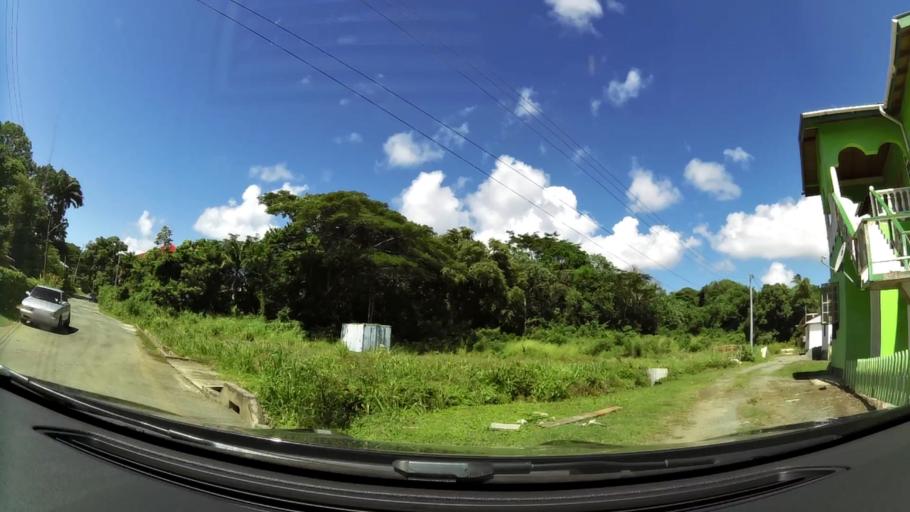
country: TT
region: Tobago
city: Scarborough
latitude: 11.1759
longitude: -60.7837
